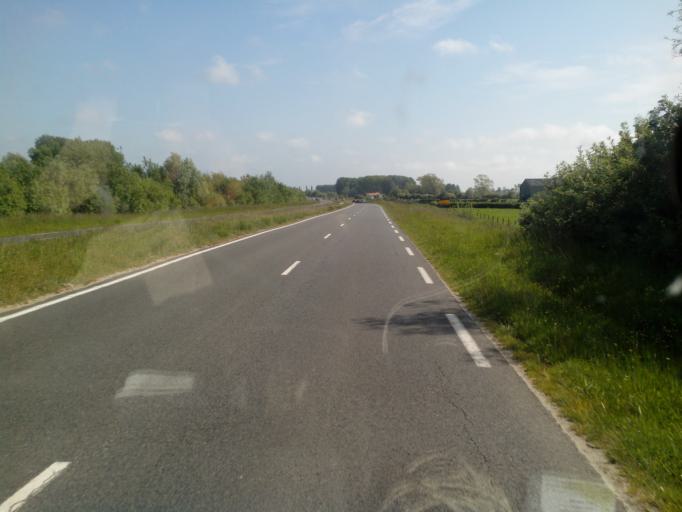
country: FR
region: Picardie
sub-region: Departement de la Somme
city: Quend
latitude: 50.2921
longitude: 1.6512
